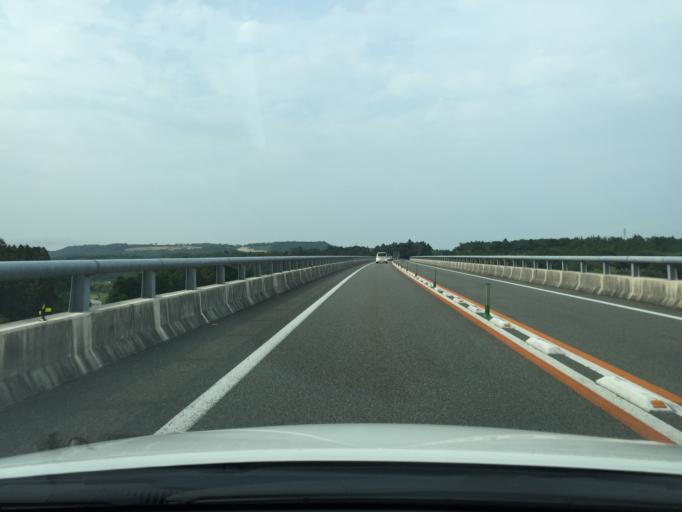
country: JP
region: Fukushima
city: Namie
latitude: 37.2904
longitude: 140.9826
